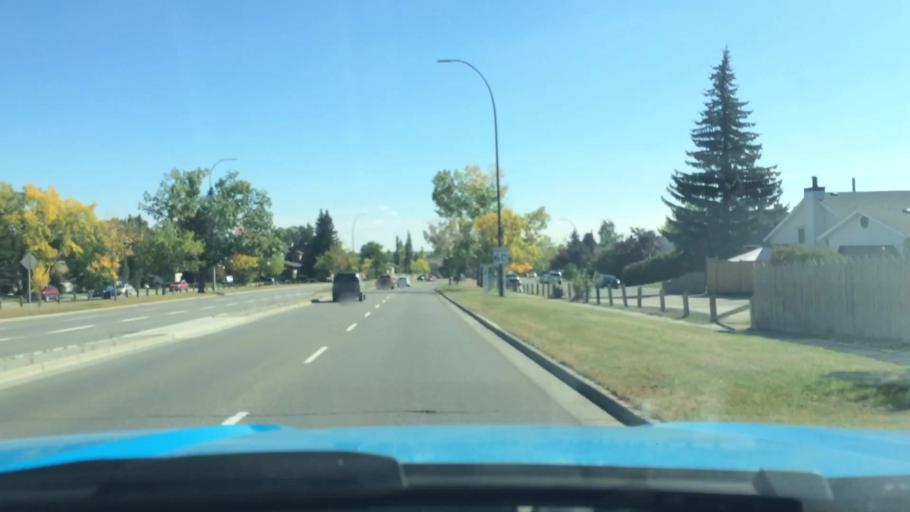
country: CA
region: Alberta
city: Calgary
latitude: 50.9140
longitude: -114.0825
